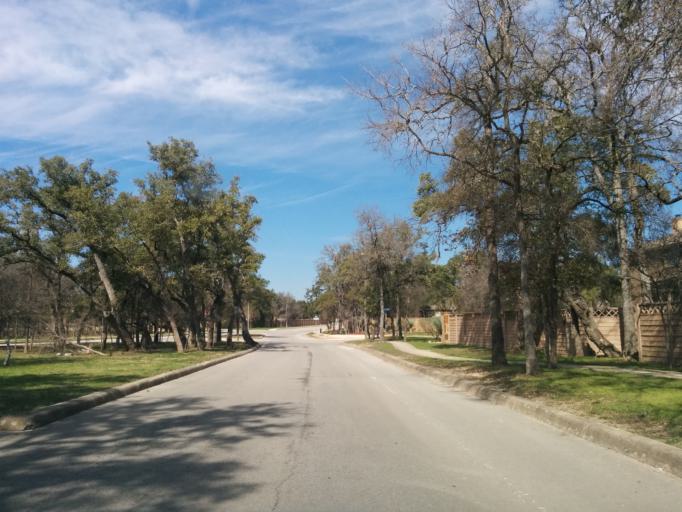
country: US
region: Texas
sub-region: Bexar County
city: Cross Mountain
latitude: 29.6695
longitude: -98.6407
